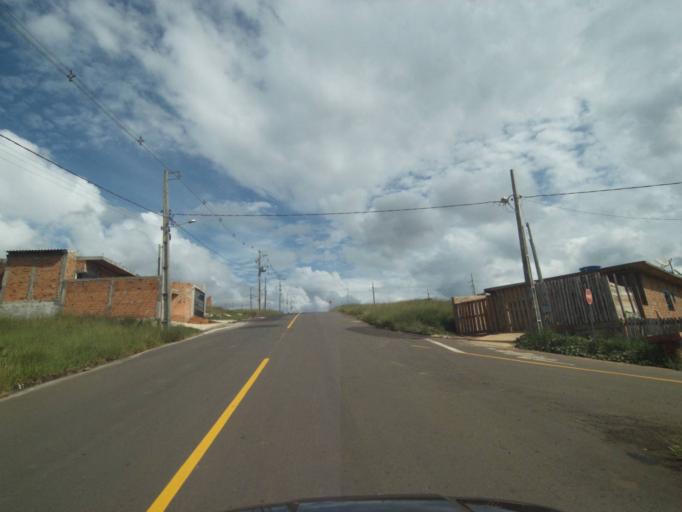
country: BR
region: Parana
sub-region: Telemaco Borba
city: Telemaco Borba
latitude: -24.3089
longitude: -50.6399
